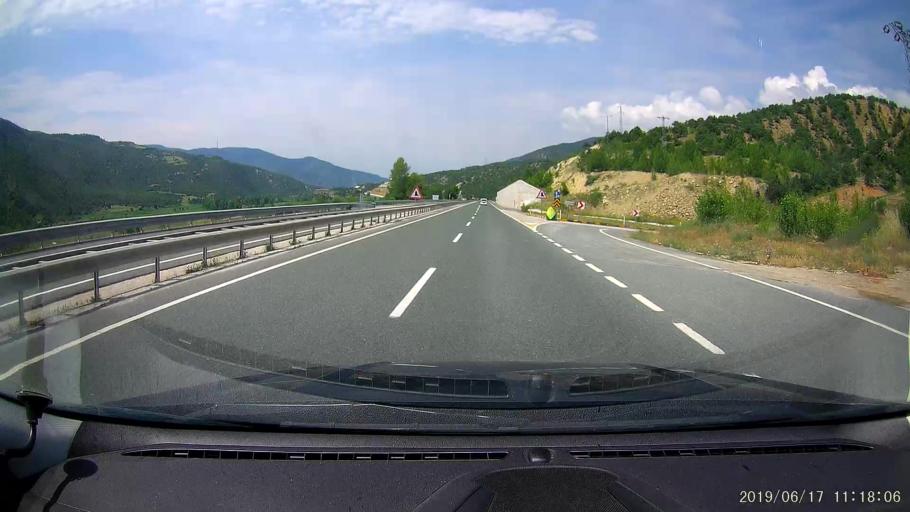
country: TR
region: Cankiri
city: Yaprakli
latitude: 40.9382
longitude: 33.8581
